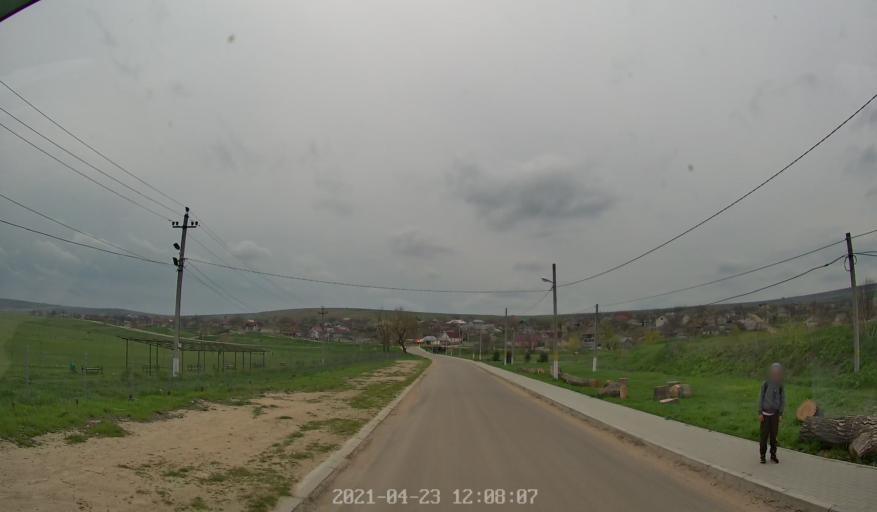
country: MD
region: Chisinau
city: Vadul lui Voda
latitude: 47.1222
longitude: 29.0017
